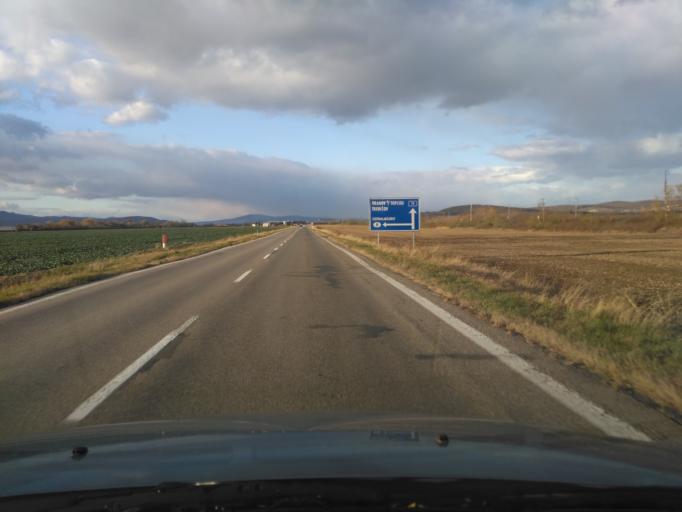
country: HU
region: Borsod-Abauj-Zemplen
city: Satoraljaujhely
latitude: 48.4214
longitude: 21.6623
